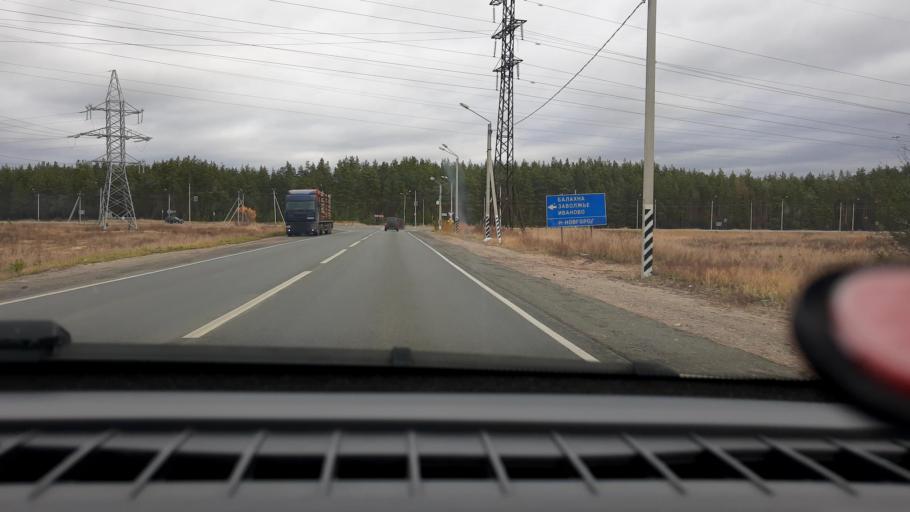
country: RU
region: Nizjnij Novgorod
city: Lukino
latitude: 56.4011
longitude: 43.6536
